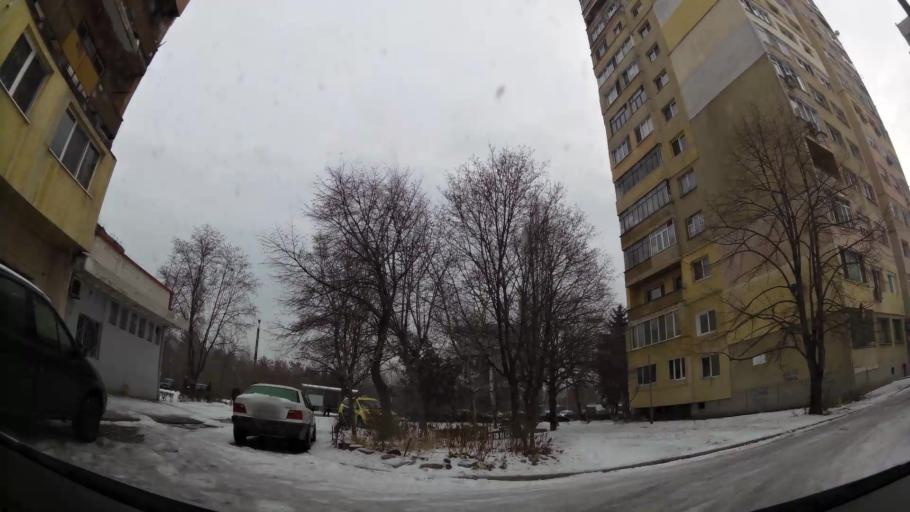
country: BG
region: Sofia-Capital
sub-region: Stolichna Obshtina
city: Sofia
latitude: 42.7178
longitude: 23.2913
